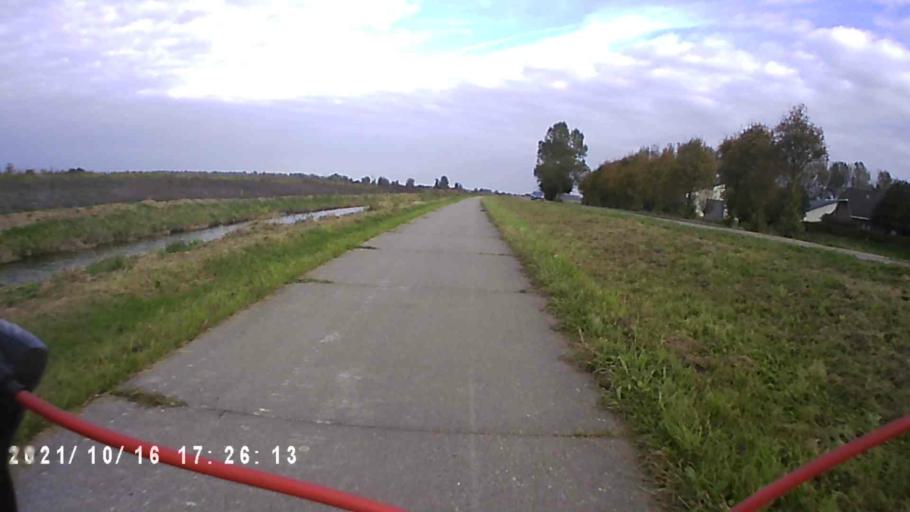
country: NL
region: Friesland
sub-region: Gemeente Kollumerland en Nieuwkruisland
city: Kollum
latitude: 53.3208
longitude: 6.1934
